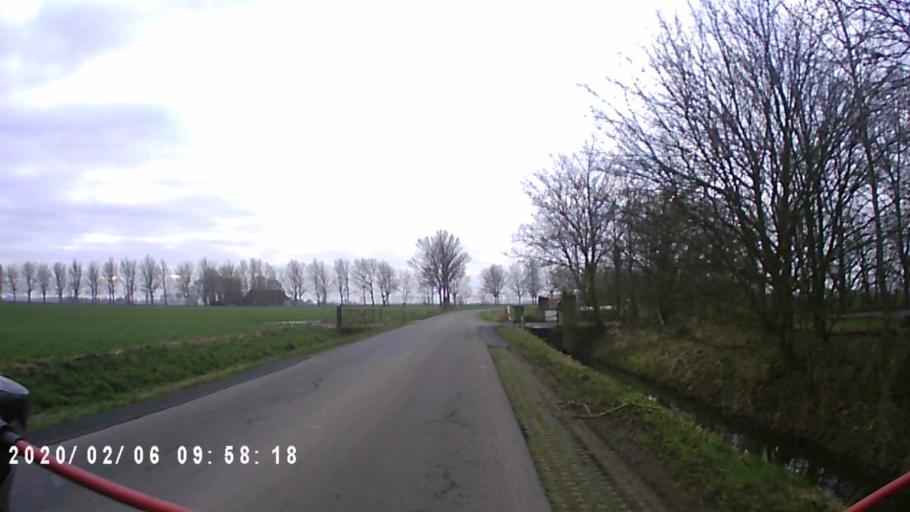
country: NL
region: Groningen
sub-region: Gemeente Zuidhorn
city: Aduard
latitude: 53.2718
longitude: 6.4962
